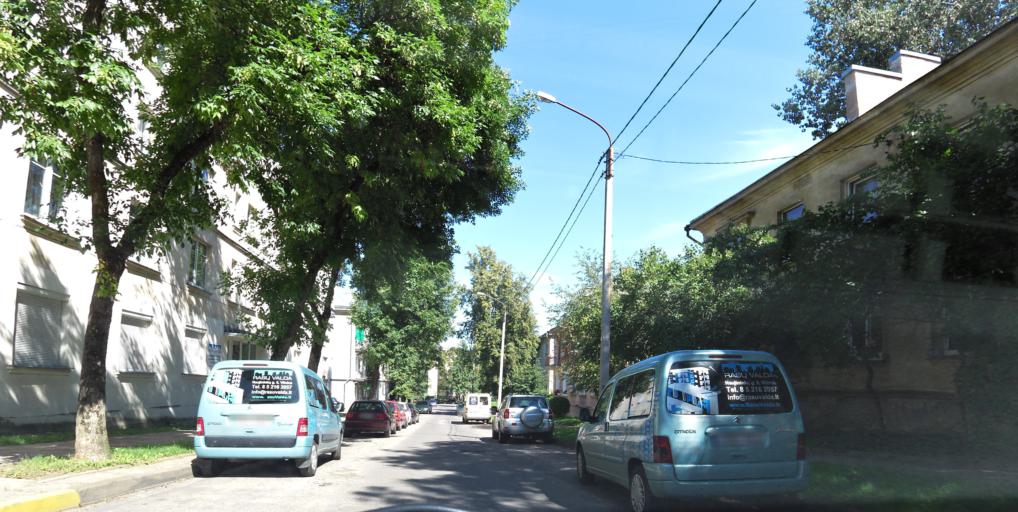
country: LT
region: Vilnius County
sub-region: Vilnius
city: Vilnius
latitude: 54.6676
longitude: 25.2895
